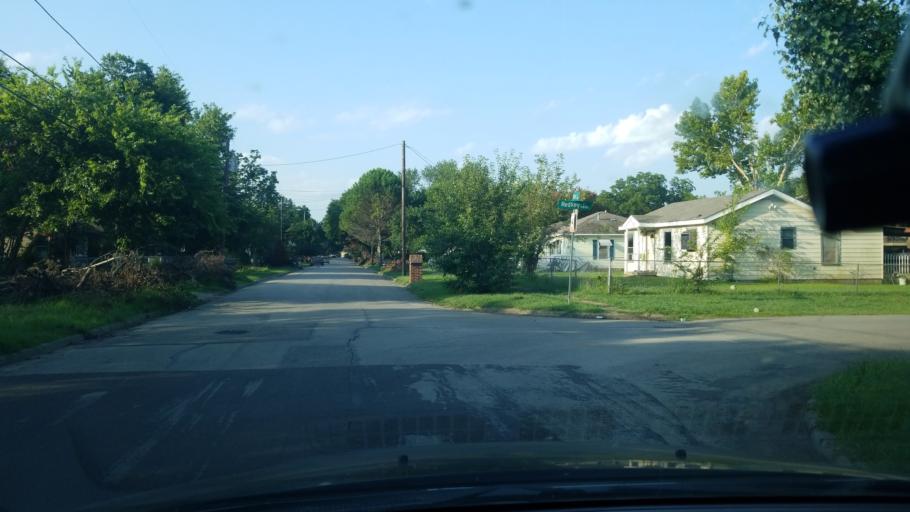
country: US
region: Texas
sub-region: Dallas County
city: Balch Springs
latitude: 32.7156
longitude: -96.6751
